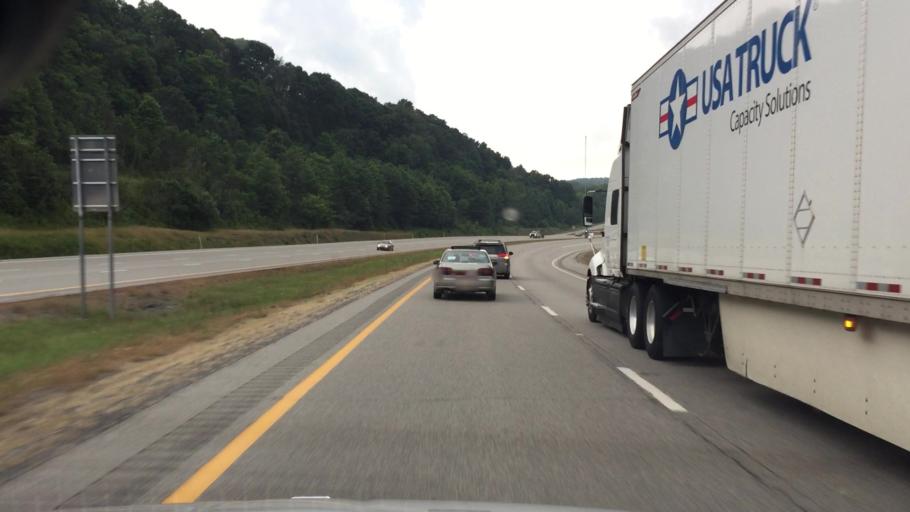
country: US
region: West Virginia
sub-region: Preston County
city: Kingwood
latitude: 39.6567
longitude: -79.6312
